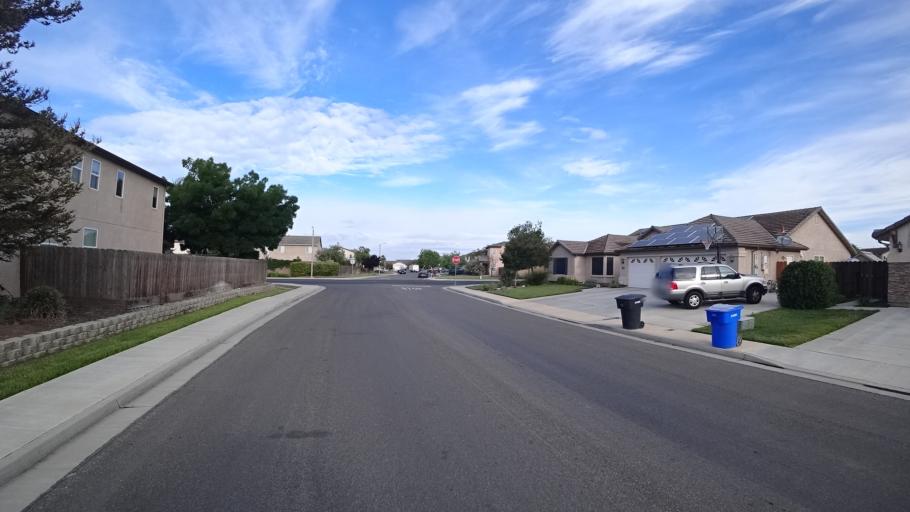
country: US
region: California
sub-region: Kings County
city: Lucerne
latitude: 36.3469
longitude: -119.6778
